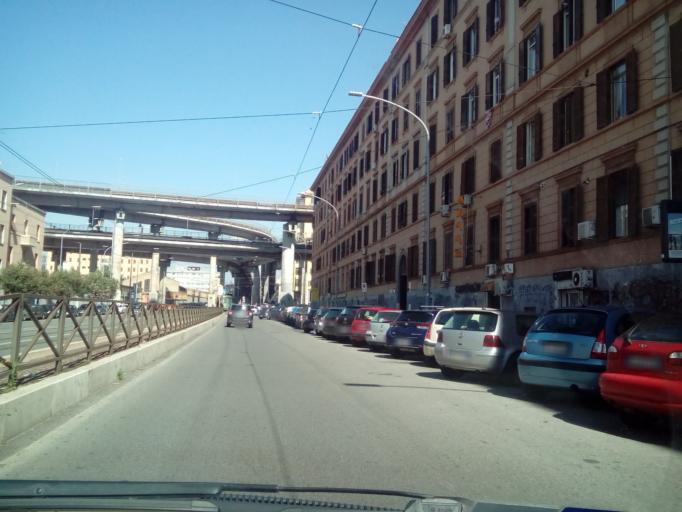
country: IT
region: Latium
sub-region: Citta metropolitana di Roma Capitale
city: Rome
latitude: 41.8914
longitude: 12.5191
